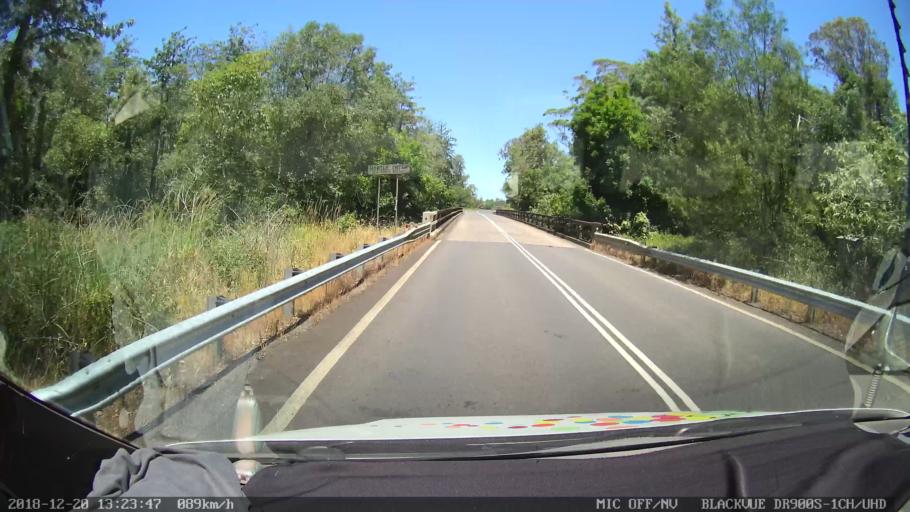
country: AU
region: New South Wales
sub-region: Richmond Valley
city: Casino
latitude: -29.1090
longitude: 152.9997
